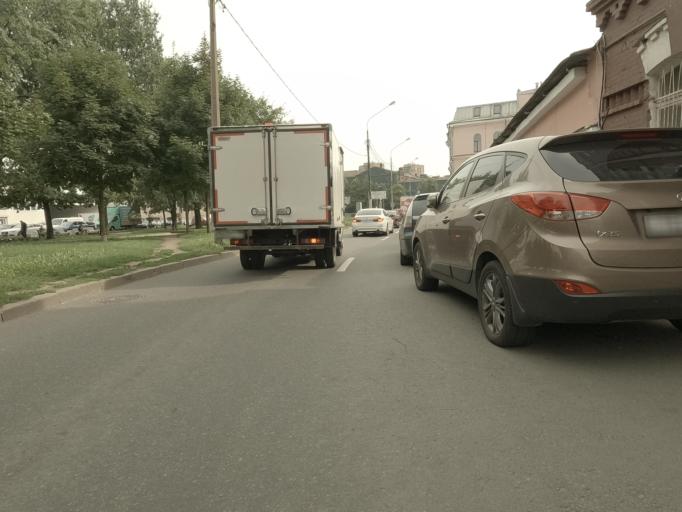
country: RU
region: St.-Petersburg
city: Admiralteisky
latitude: 59.9105
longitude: 30.2875
